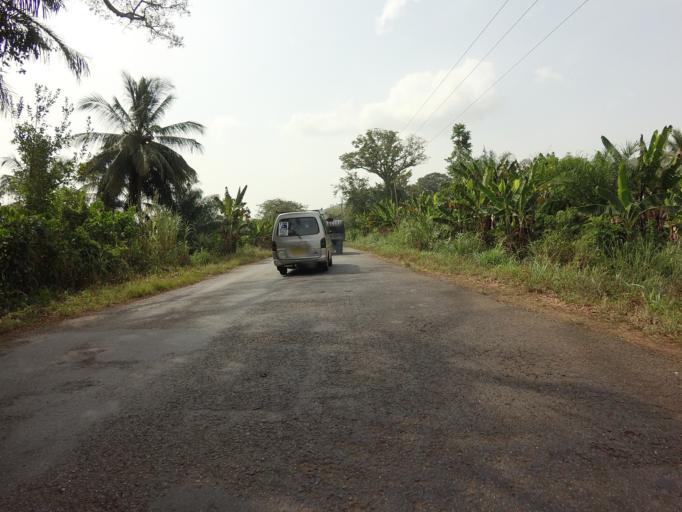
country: GH
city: Akropong
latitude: 6.2899
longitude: 0.1321
